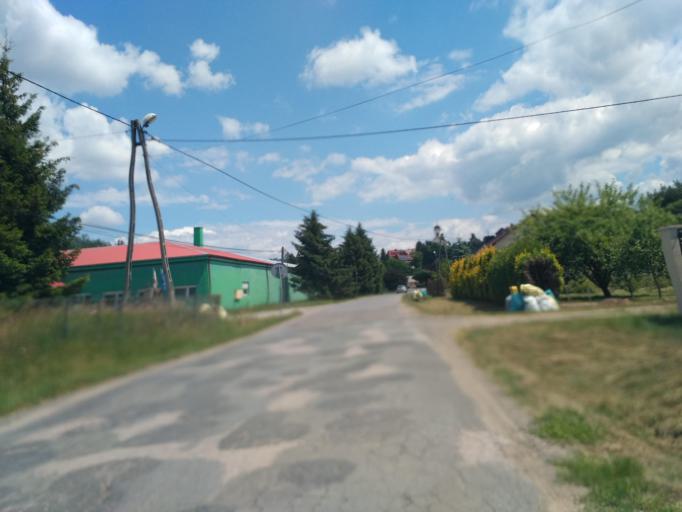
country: PL
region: Subcarpathian Voivodeship
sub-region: Powiat debicki
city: Brzostek
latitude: 49.8776
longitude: 21.4054
